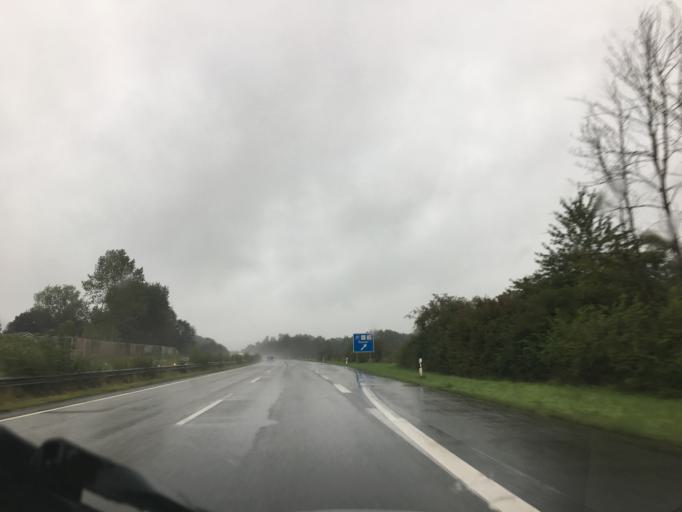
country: DE
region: Schleswig-Holstein
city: Rumohr
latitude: 54.2492
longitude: 10.0260
